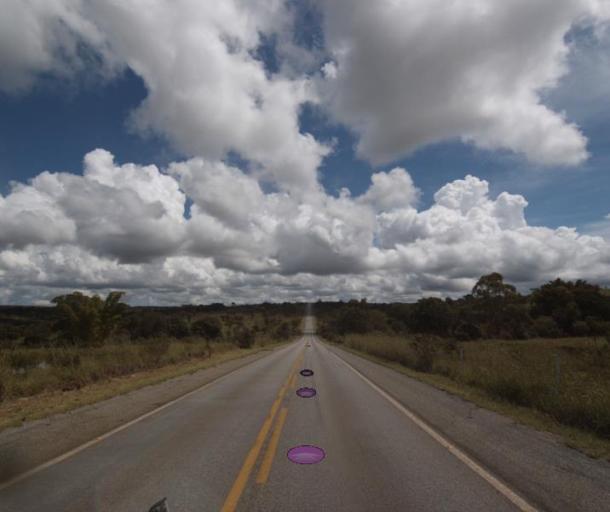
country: BR
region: Goias
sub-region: Pirenopolis
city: Pirenopolis
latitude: -15.7508
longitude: -48.6256
